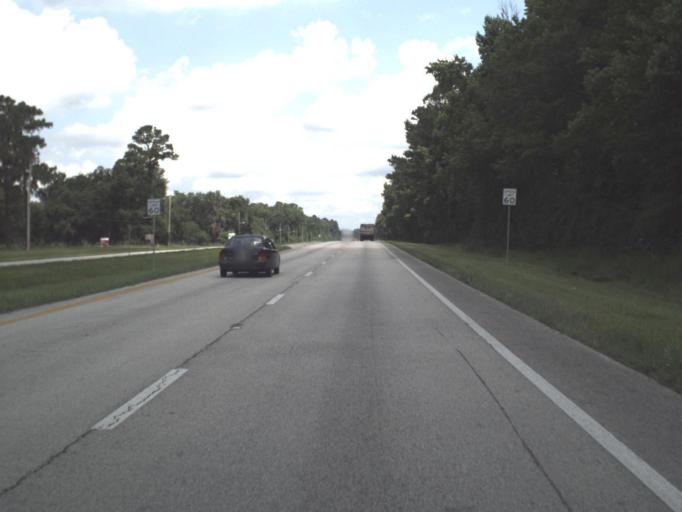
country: US
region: Florida
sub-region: Alachua County
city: Alachua
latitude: 29.7452
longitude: -82.3892
